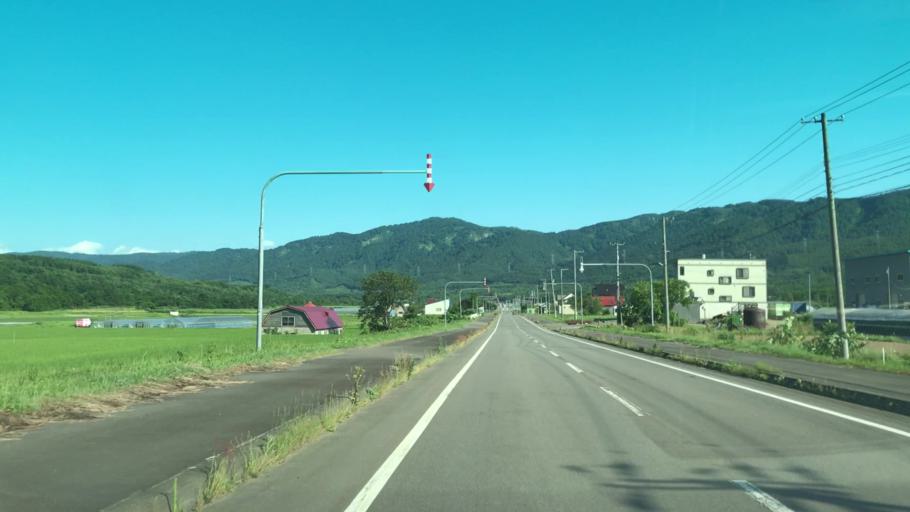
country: JP
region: Hokkaido
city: Yoichi
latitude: 43.0533
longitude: 140.7199
